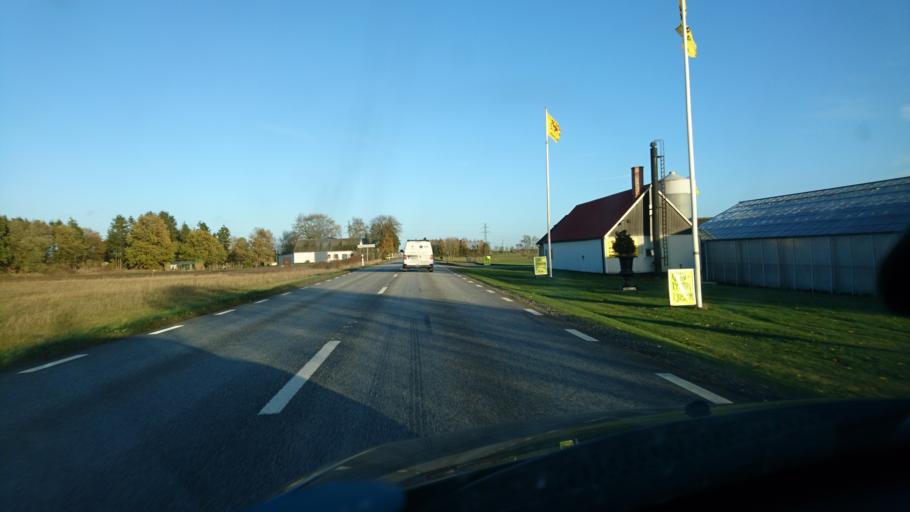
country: SE
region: Skane
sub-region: Tomelilla Kommun
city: Tomelilla
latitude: 55.5461
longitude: 13.9991
